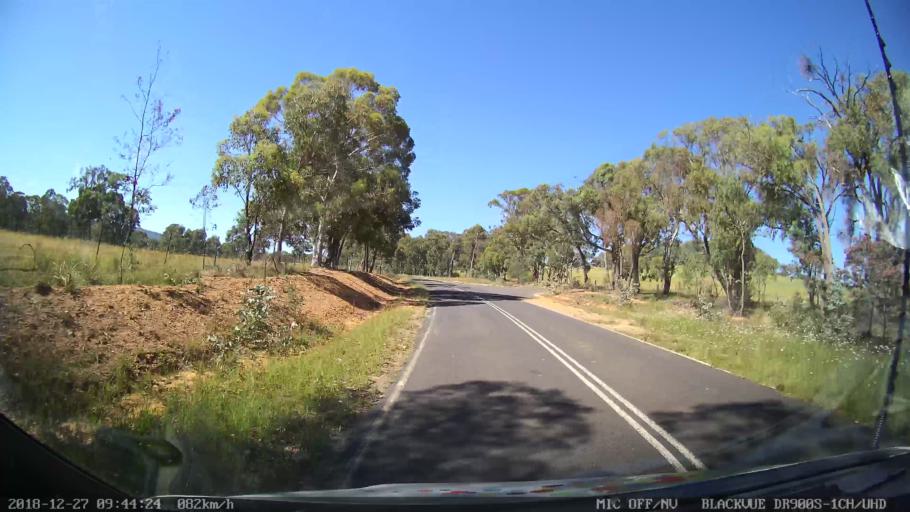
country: AU
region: New South Wales
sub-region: Lithgow
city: Portland
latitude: -33.3150
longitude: 149.9925
